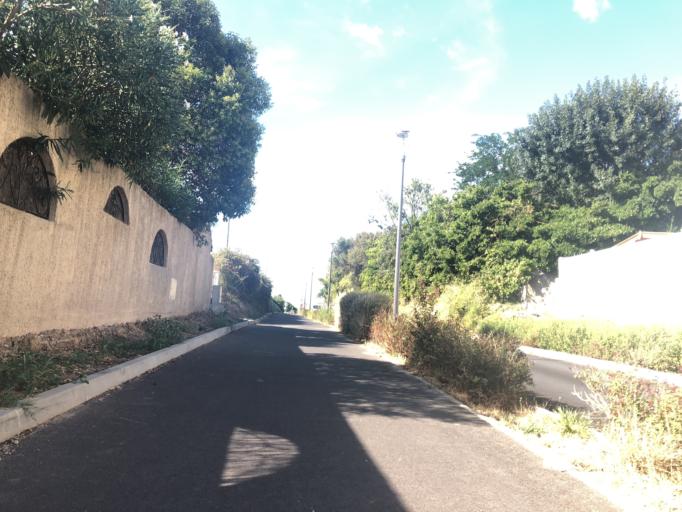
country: FR
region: Languedoc-Roussillon
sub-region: Departement de l'Herault
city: Meze
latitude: 43.4307
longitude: 3.6027
